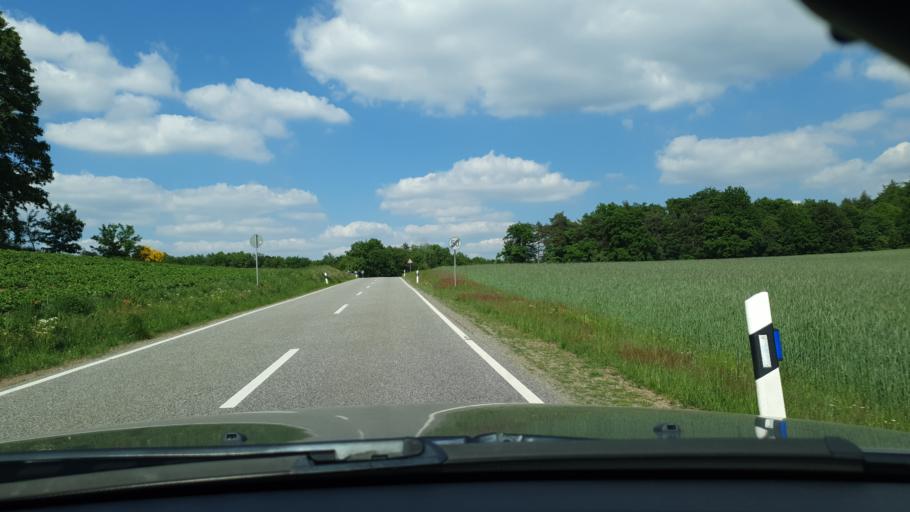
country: DE
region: Rheinland-Pfalz
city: Lambsborn
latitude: 49.3733
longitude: 7.4437
